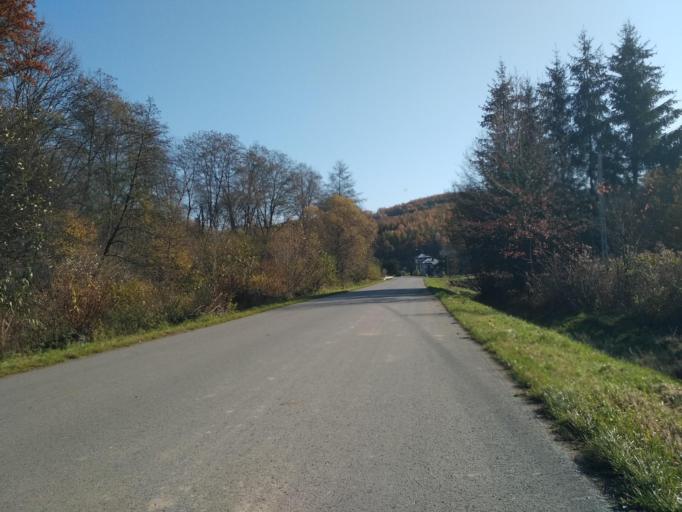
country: PL
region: Subcarpathian Voivodeship
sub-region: Powiat brzozowski
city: Nozdrzec
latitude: 49.7931
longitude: 22.1843
